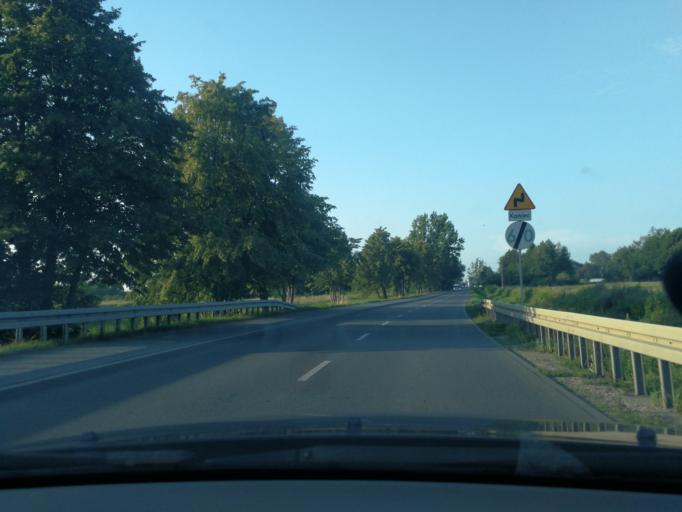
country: PL
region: Masovian Voivodeship
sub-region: Powiat warszawski zachodni
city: Ozarow Mazowiecki
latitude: 52.1861
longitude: 20.7512
